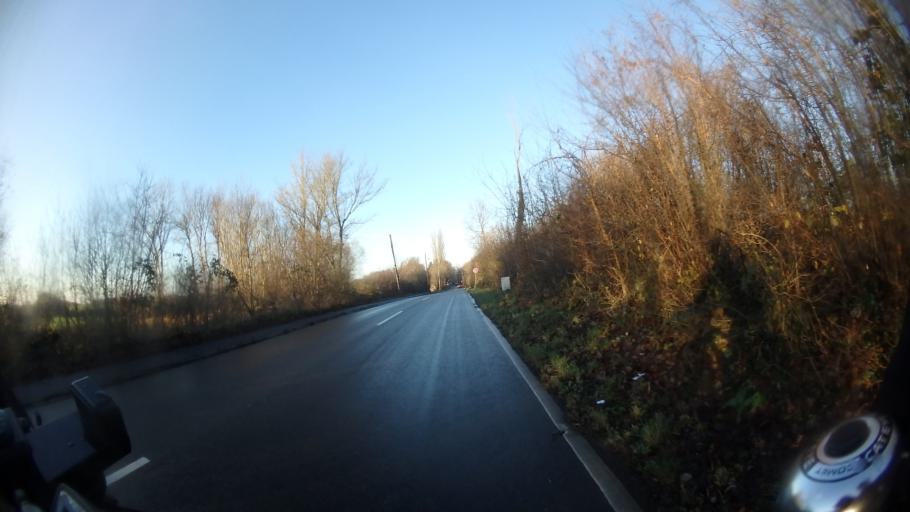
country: DE
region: Schleswig-Holstein
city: Travemuende
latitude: 53.9813
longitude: 10.8639
